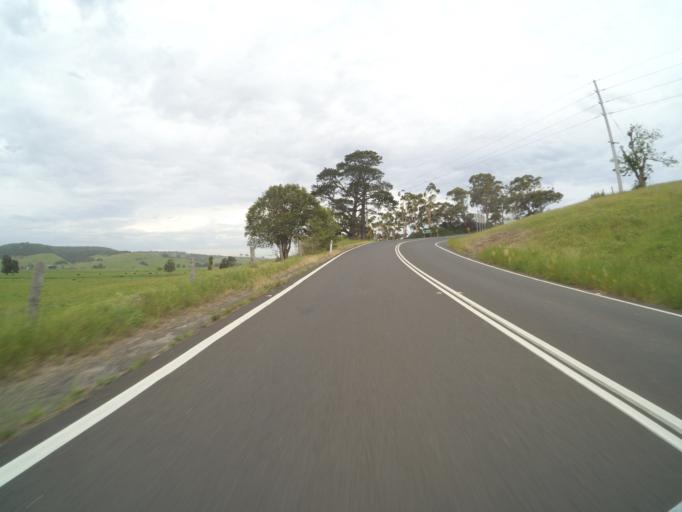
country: AU
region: New South Wales
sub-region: Kiama
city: Jamberoo
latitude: -34.6530
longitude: 150.8118
